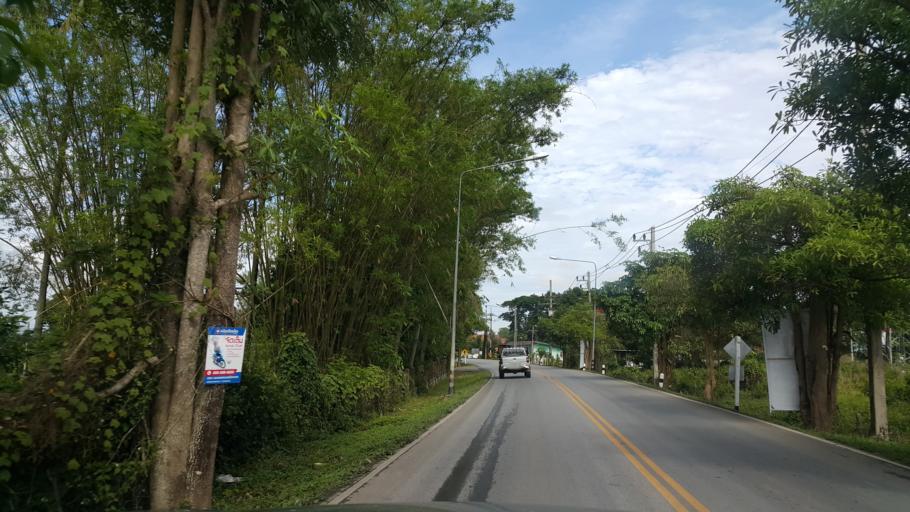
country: TH
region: Chiang Rai
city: Chiang Rai
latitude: 19.9128
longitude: 99.8715
